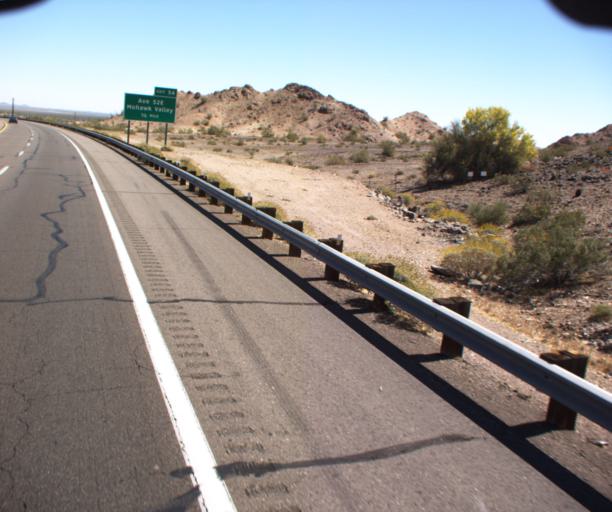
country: US
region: Arizona
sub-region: Yuma County
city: Wellton
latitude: 32.7257
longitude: -113.7444
